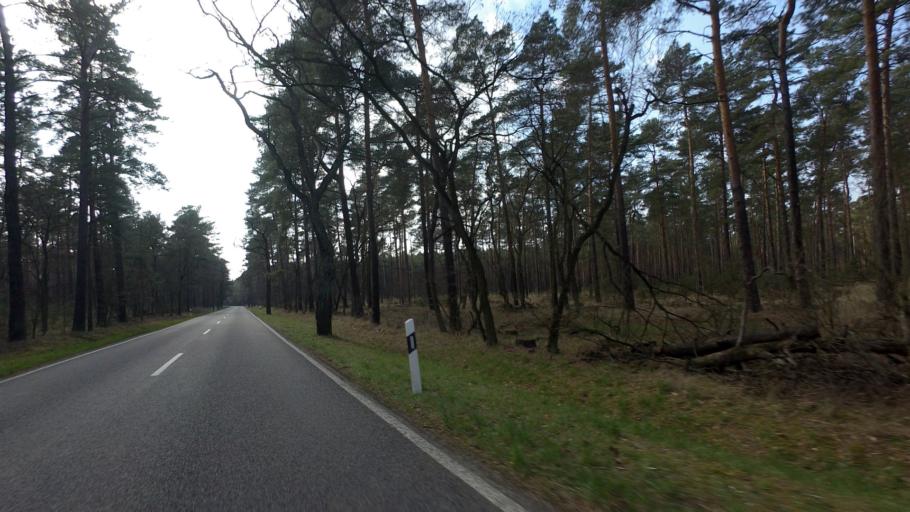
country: DE
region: Brandenburg
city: Dahme
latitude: 51.9584
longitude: 13.4227
